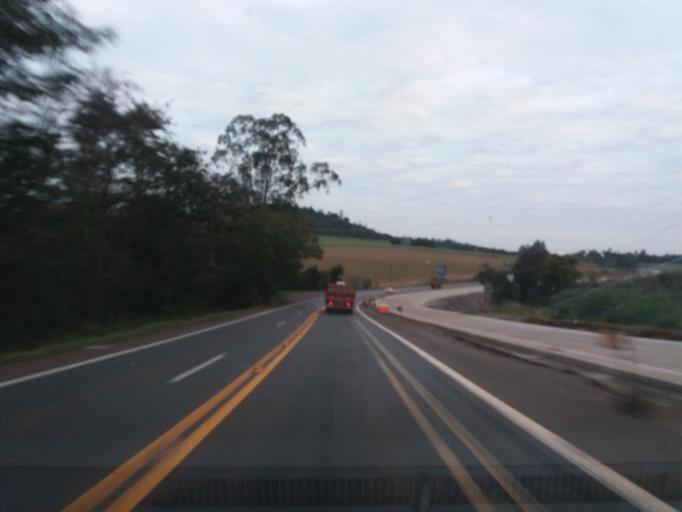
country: BR
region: Parana
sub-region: Realeza
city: Realeza
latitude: -25.3833
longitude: -53.5768
